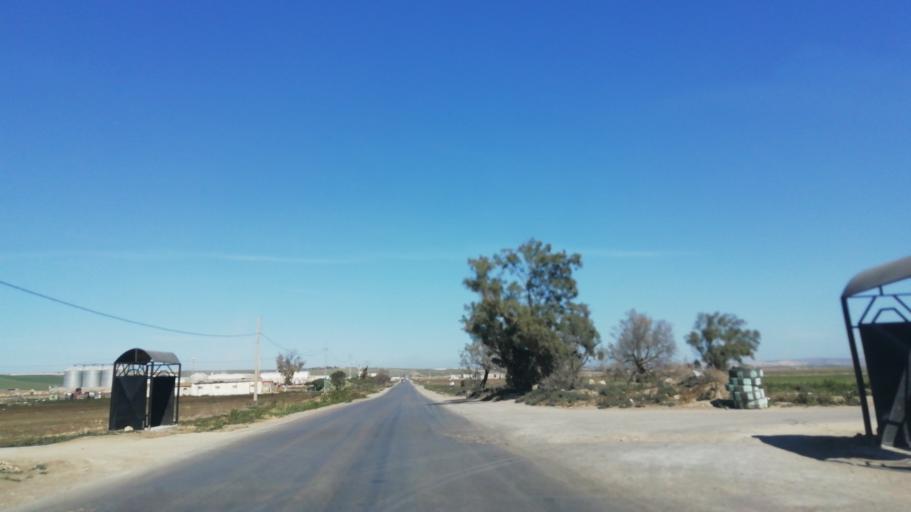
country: DZ
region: Oran
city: Es Senia
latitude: 35.5151
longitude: -0.5893
